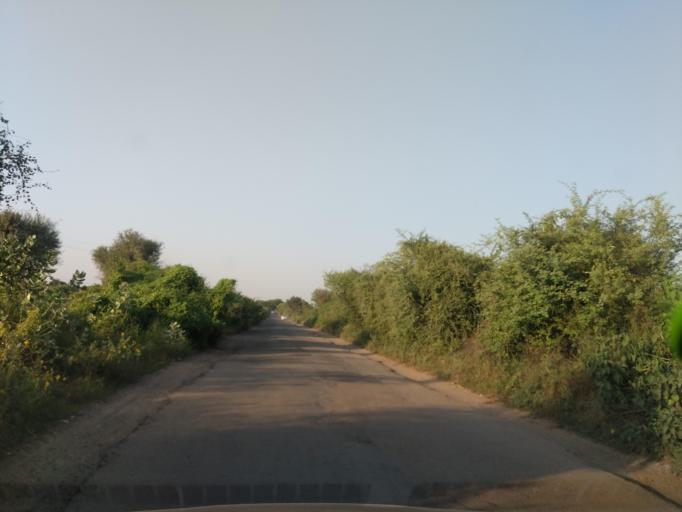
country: IN
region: Rajasthan
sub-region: Churu
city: Rajgarh
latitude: 28.5821
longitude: 75.3729
